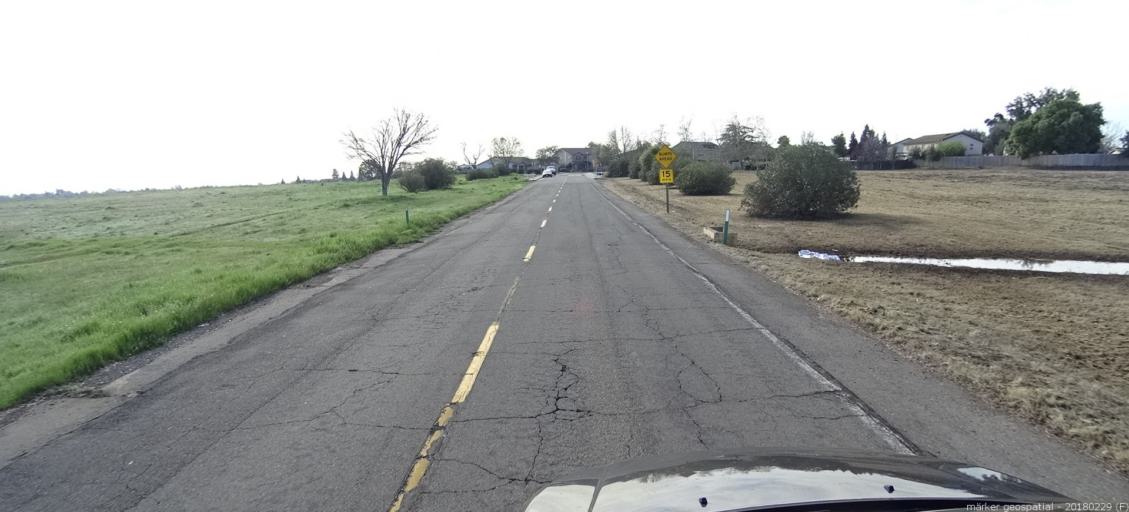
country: US
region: California
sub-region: Sacramento County
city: Rancho Cordova
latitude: 38.5499
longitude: -121.2775
